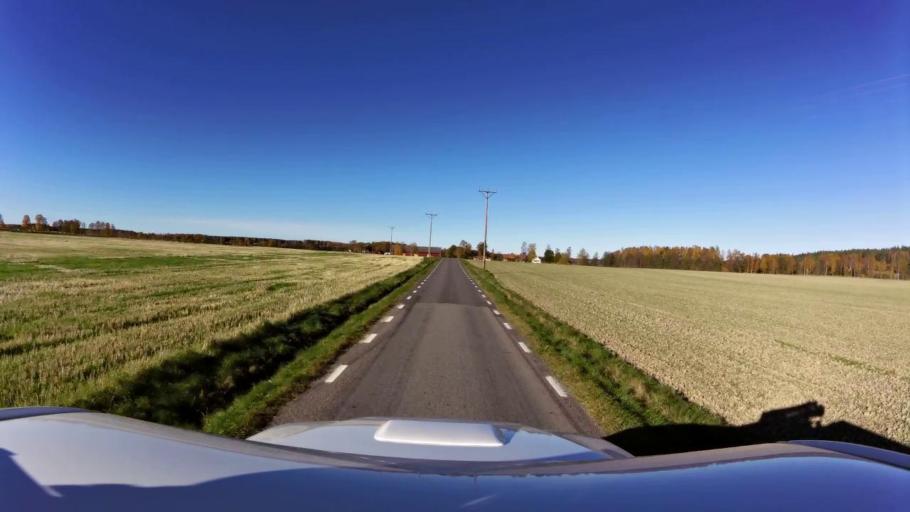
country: SE
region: OEstergoetland
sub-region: Linkopings Kommun
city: Ljungsbro
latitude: 58.5354
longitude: 15.4143
